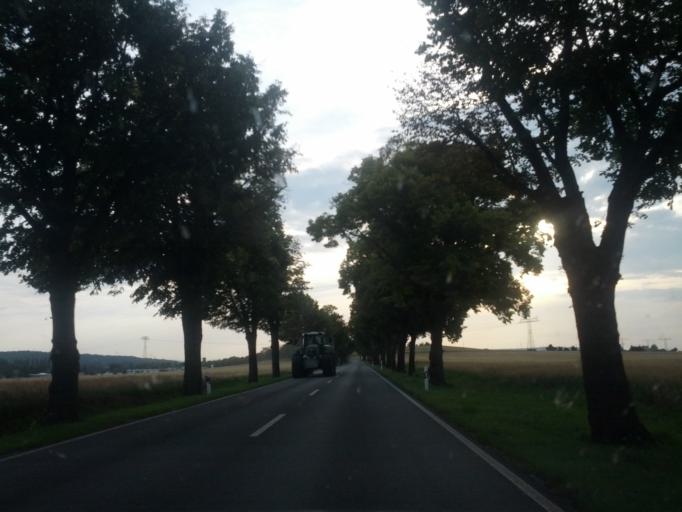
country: DE
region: Thuringia
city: Tuttleben
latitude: 50.9461
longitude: 10.7668
